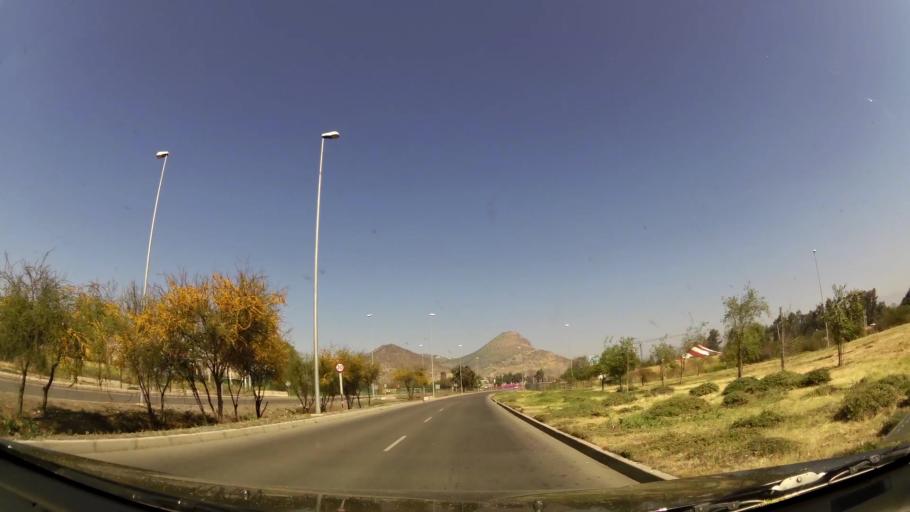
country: CL
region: Santiago Metropolitan
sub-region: Provincia de Chacabuco
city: Chicureo Abajo
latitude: -33.3018
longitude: -70.6616
